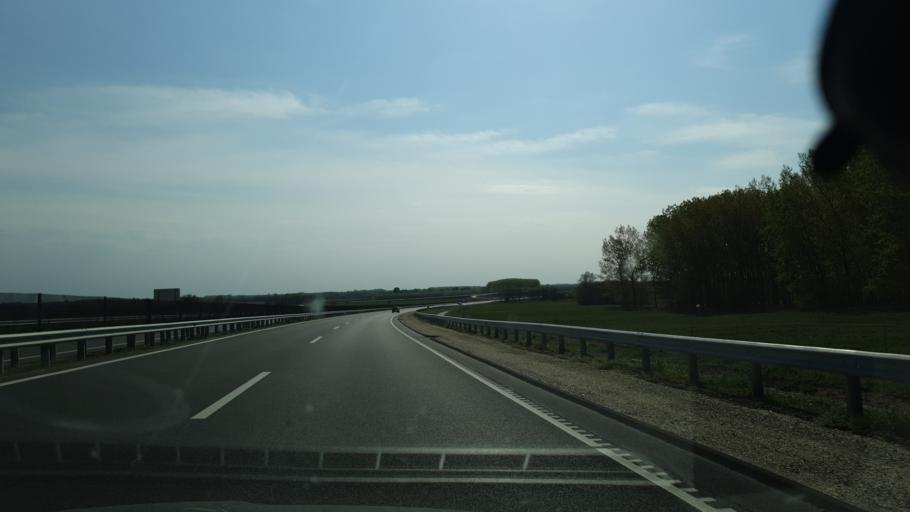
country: HU
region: Pest
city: Monor
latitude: 47.3749
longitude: 19.4330
